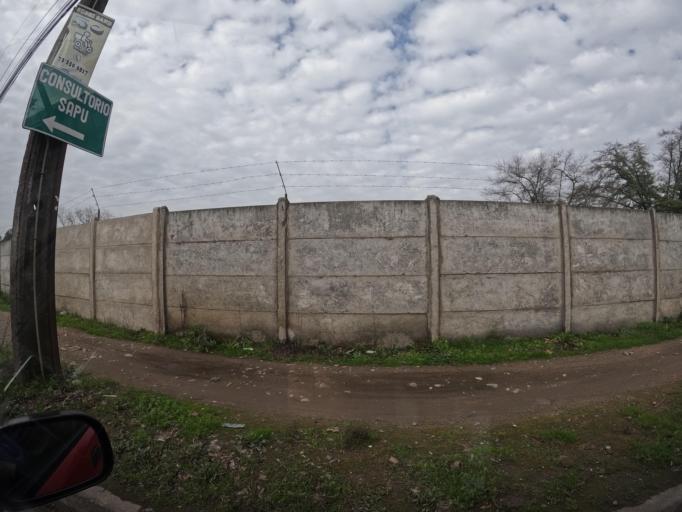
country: CL
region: Maule
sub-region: Provincia de Linares
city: Linares
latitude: -35.8371
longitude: -71.5932
